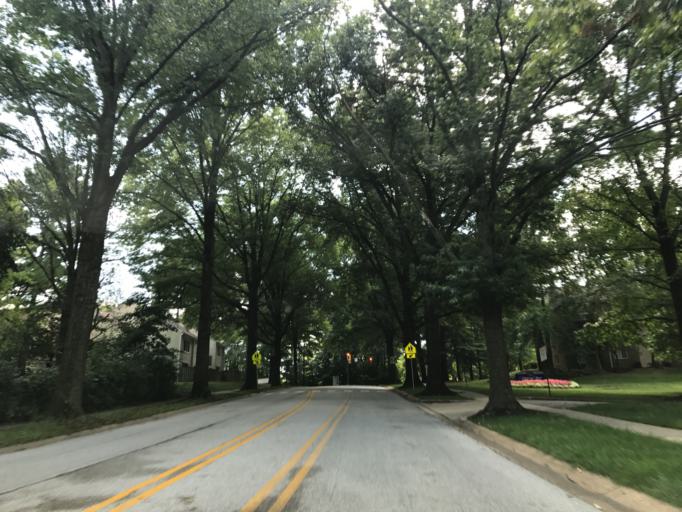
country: US
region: Maryland
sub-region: Howard County
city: Columbia
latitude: 39.2230
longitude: -76.8849
